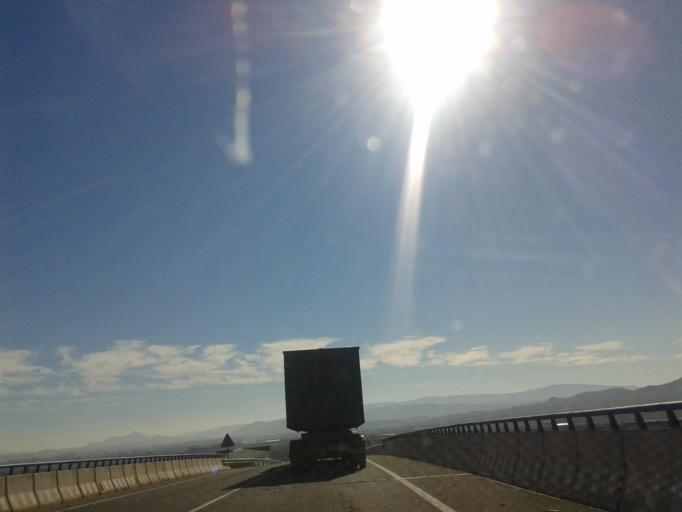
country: ES
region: Castille-La Mancha
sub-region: Provincia de Albacete
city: Caudete
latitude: 38.7171
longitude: -0.9676
